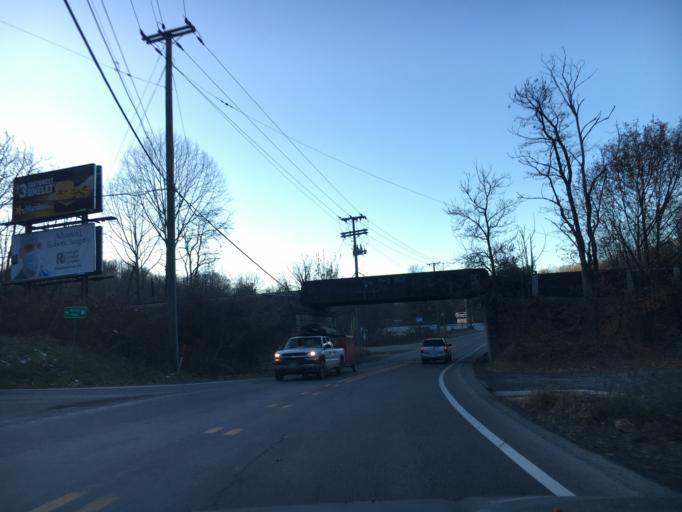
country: US
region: West Virginia
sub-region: Raleigh County
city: Beaver
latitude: 37.7565
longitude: -81.1559
